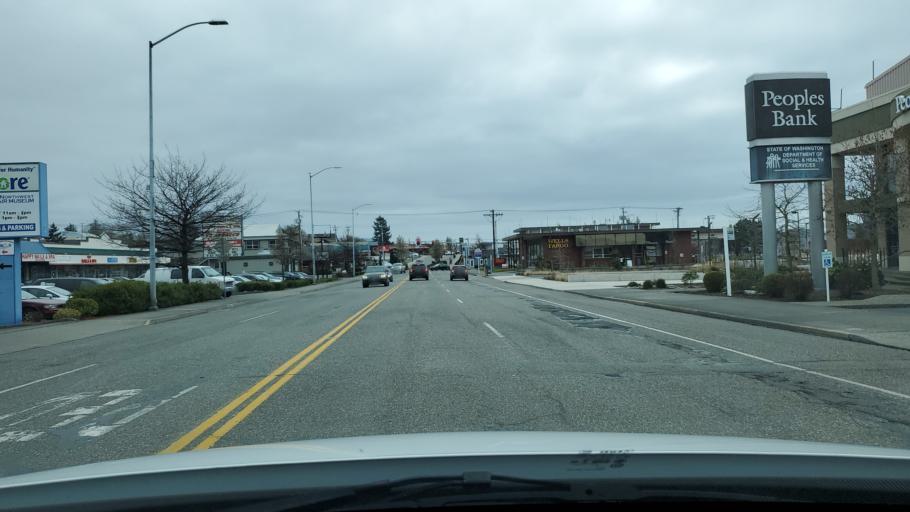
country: US
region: Washington
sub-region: Island County
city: Oak Harbor
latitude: 48.2877
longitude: -122.6546
